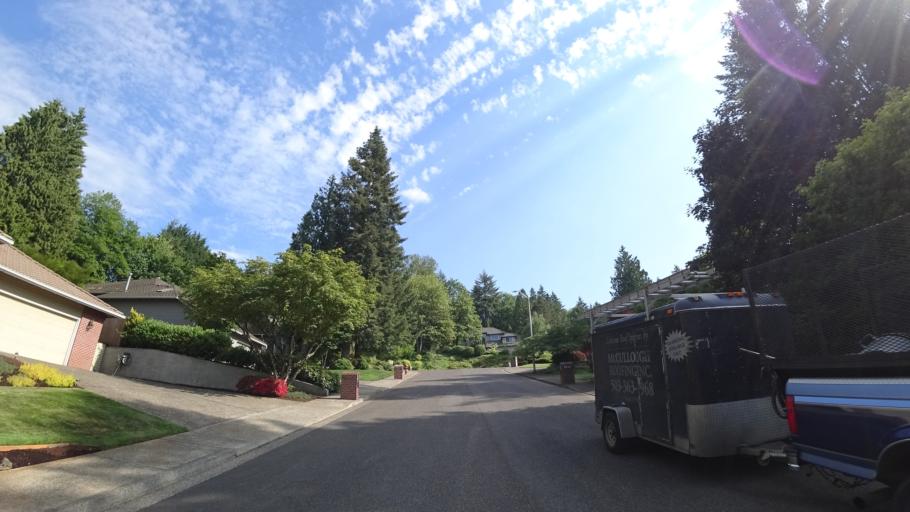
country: US
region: Oregon
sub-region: Washington County
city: Garden Home-Whitford
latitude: 45.4598
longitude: -122.7397
